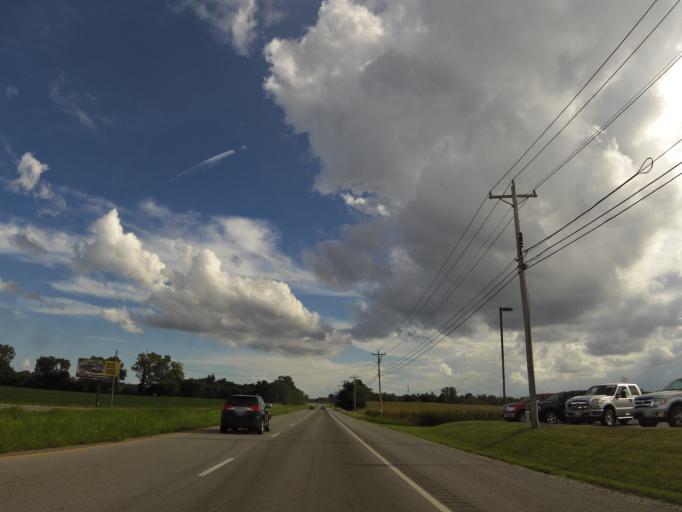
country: US
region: Kentucky
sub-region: Christian County
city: Hopkinsville
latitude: 36.8006
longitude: -87.4722
